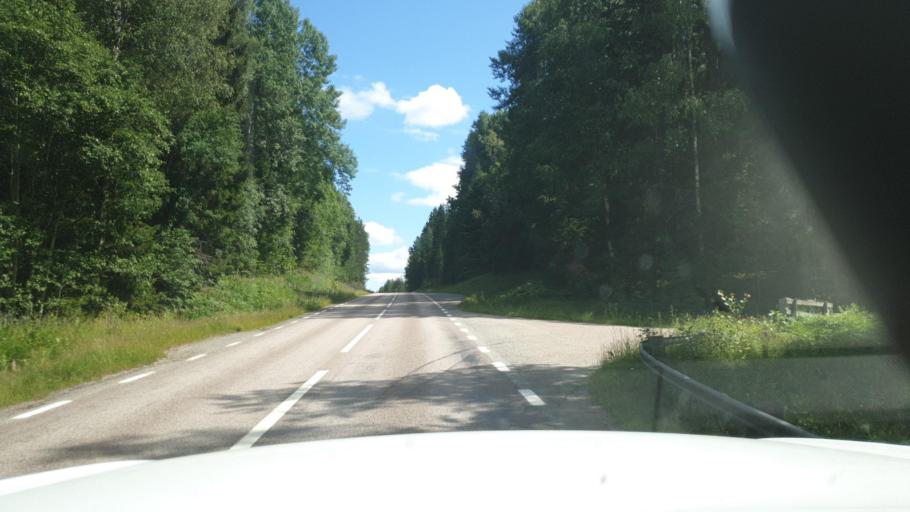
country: SE
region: Vaermland
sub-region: Eda Kommun
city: Amotfors
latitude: 59.7024
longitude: 12.3122
